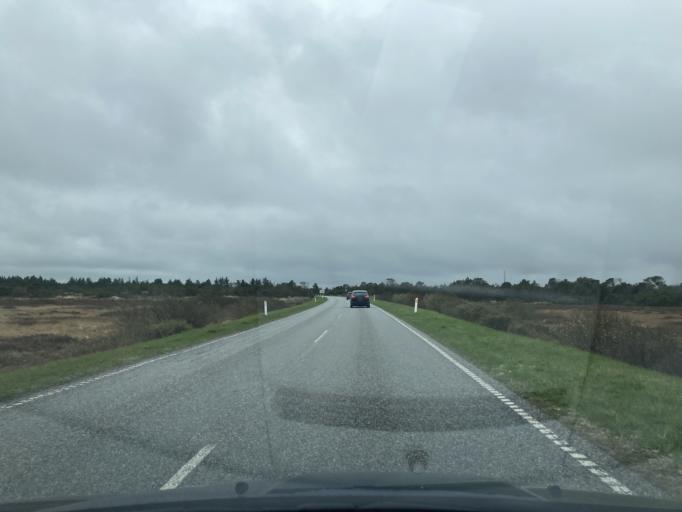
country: DK
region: North Denmark
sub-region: Thisted Kommune
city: Hurup
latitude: 56.9249
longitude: 8.3753
